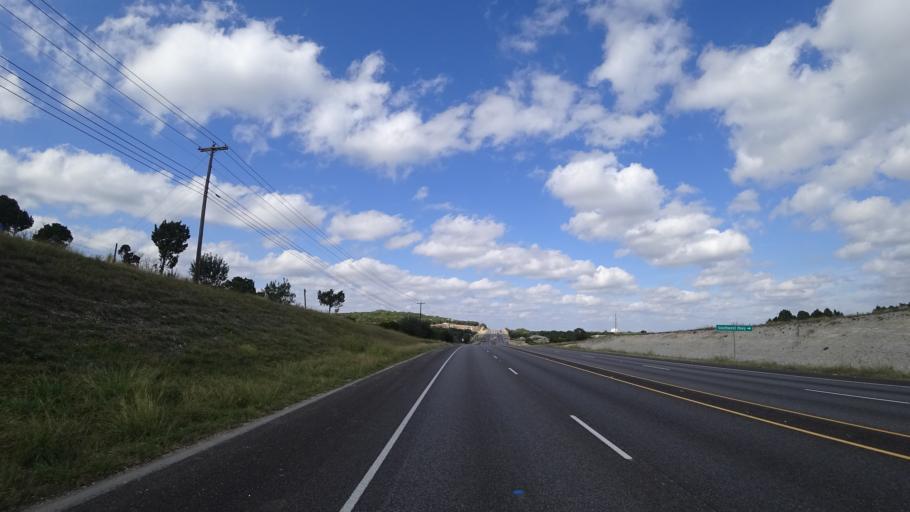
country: US
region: Texas
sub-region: Travis County
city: Barton Creek
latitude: 30.2724
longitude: -97.9126
